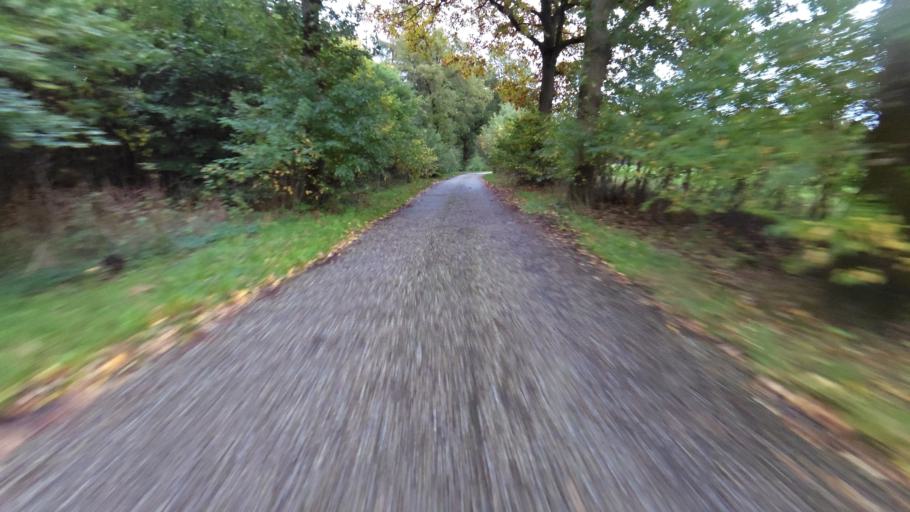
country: NL
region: Gelderland
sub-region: Gemeente Renkum
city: Oosterbeek
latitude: 52.0056
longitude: 5.8383
